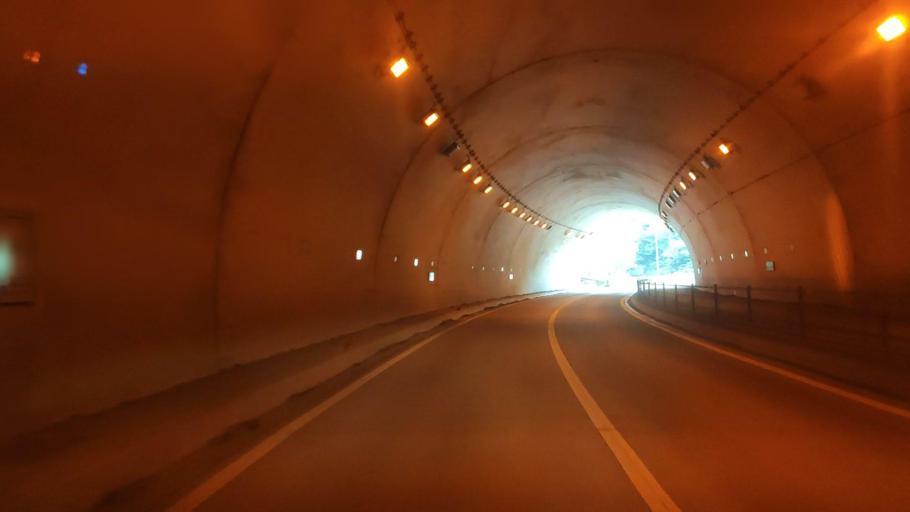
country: JP
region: Kumamoto
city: Hitoyoshi
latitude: 32.3874
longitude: 130.8350
